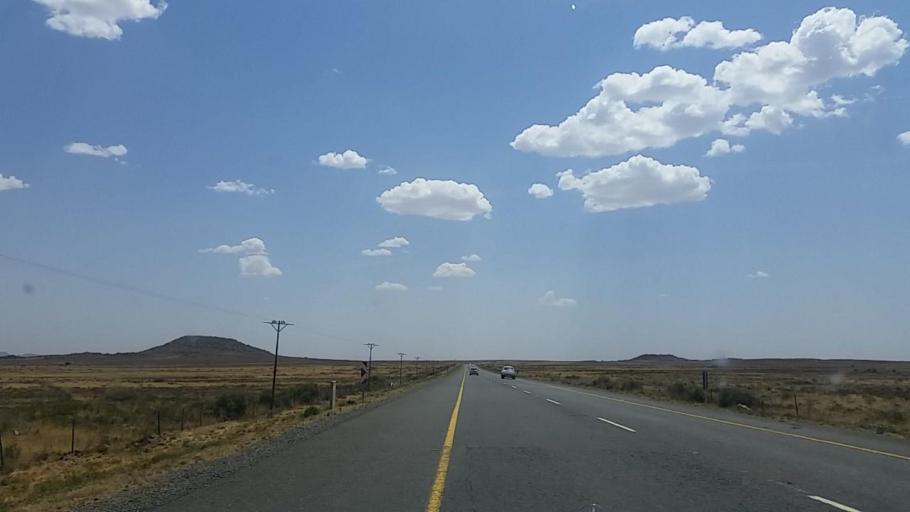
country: ZA
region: Northern Cape
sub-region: Pixley ka Seme District Municipality
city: Noupoort
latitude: -31.1167
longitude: 24.9563
